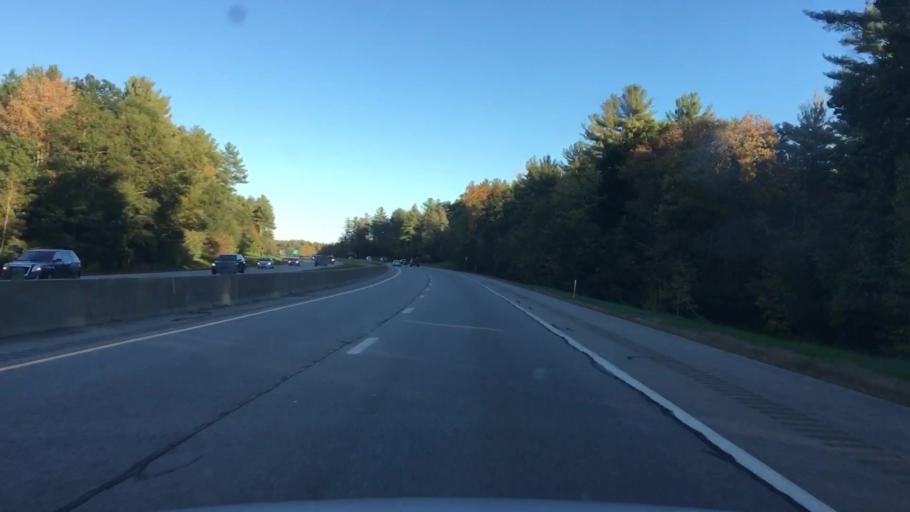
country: US
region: New Hampshire
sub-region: Rockingham County
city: Exeter
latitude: 43.0080
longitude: -71.0009
